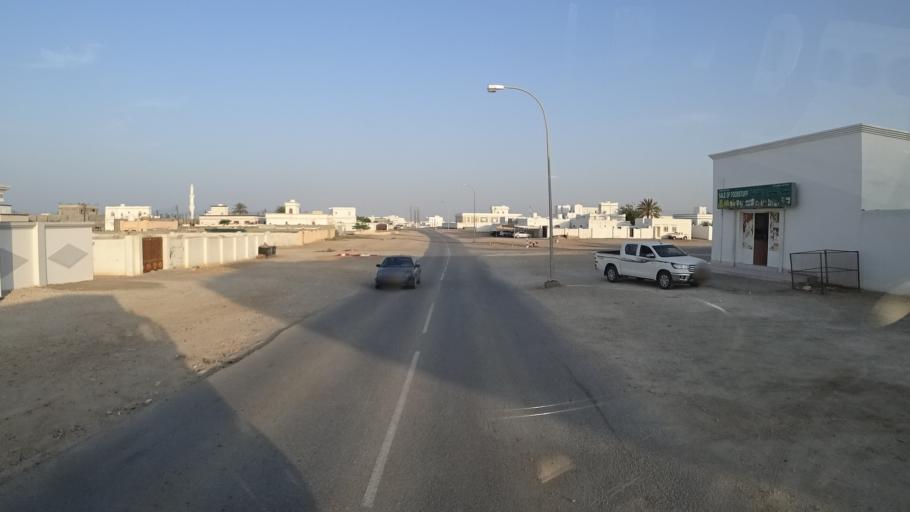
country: OM
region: Ash Sharqiyah
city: Sur
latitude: 22.6123
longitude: 59.4650
